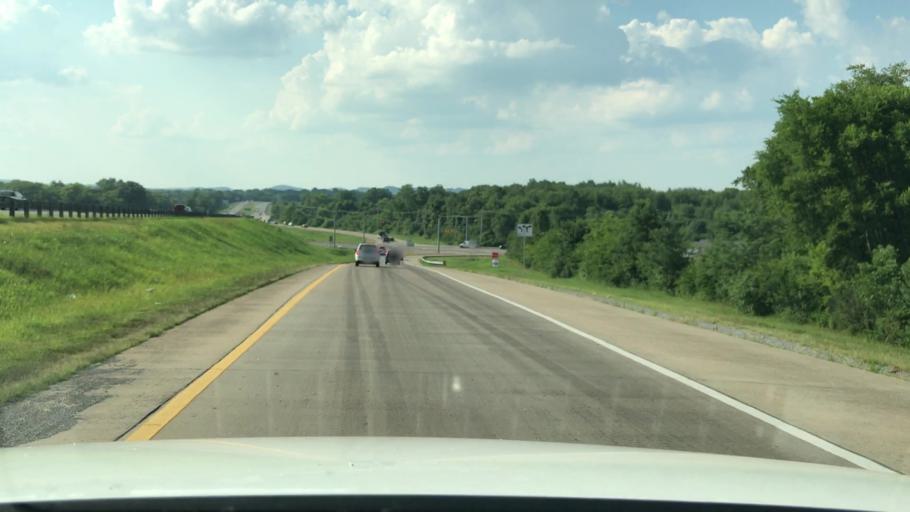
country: US
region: Tennessee
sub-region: Sumner County
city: Gallatin
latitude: 36.3858
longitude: -86.4730
